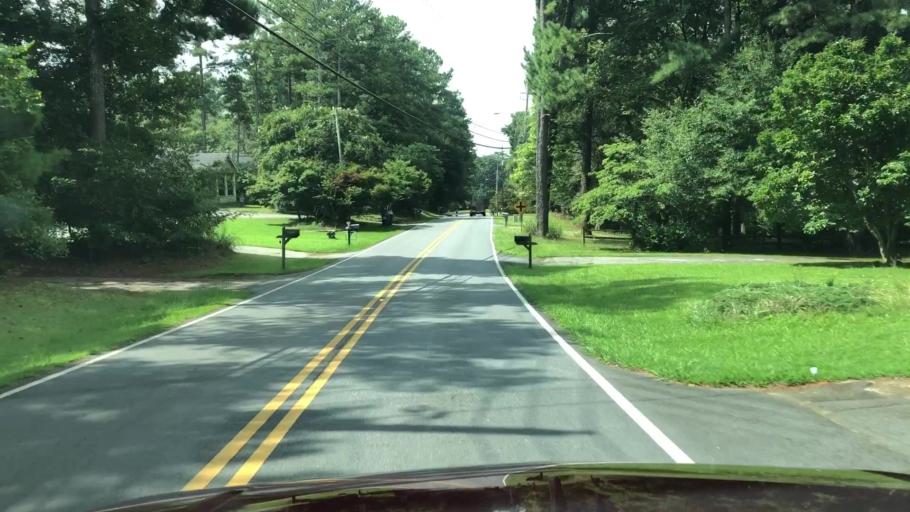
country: US
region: Georgia
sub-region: Cherokee County
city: Woodstock
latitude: 34.1487
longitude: -84.6020
